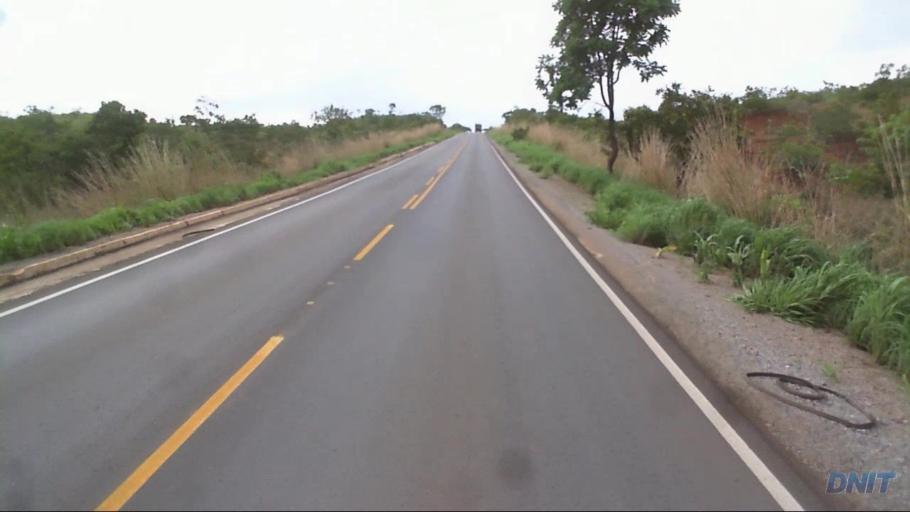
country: BR
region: Goias
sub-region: Padre Bernardo
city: Padre Bernardo
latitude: -15.2035
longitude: -48.2829
